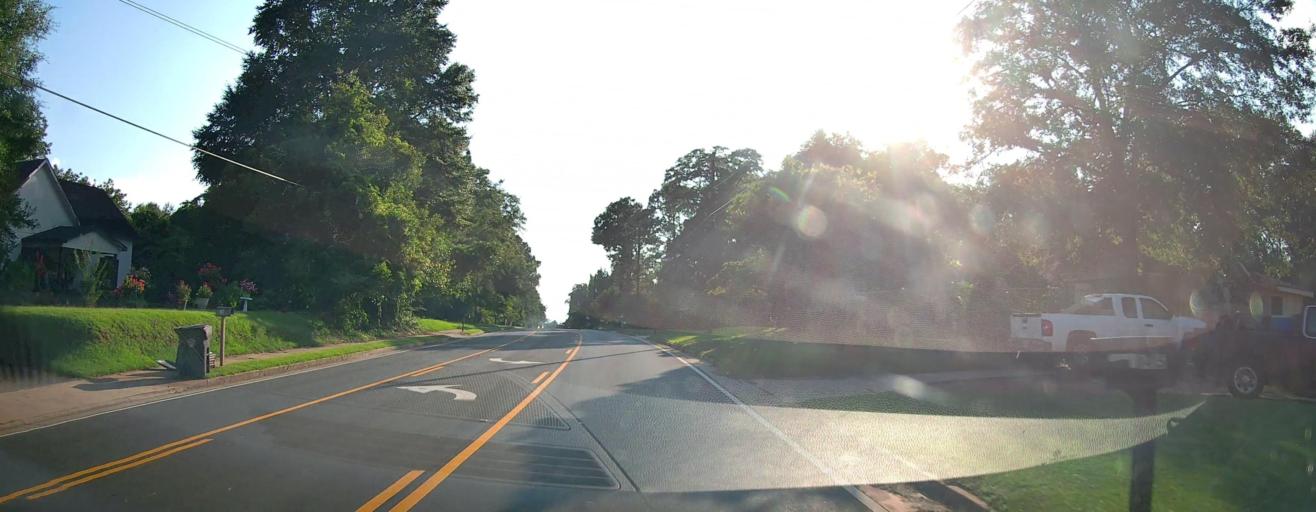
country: US
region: Georgia
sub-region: Houston County
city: Perry
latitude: 32.4627
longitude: -83.7235
